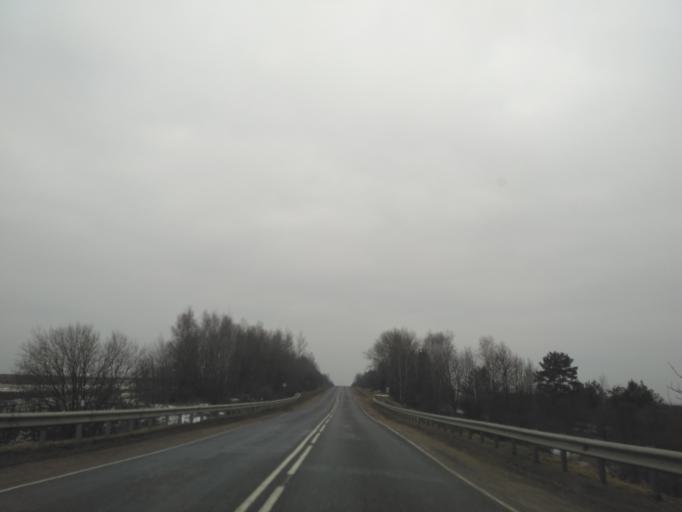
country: BY
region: Minsk
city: Snow
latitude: 53.3143
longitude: 26.4246
